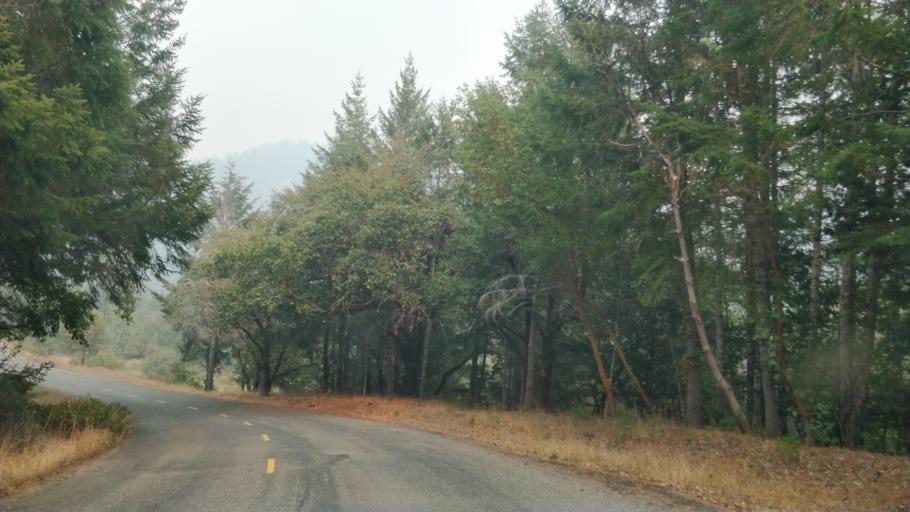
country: US
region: California
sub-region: Humboldt County
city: Rio Dell
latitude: 40.3317
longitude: -124.0291
